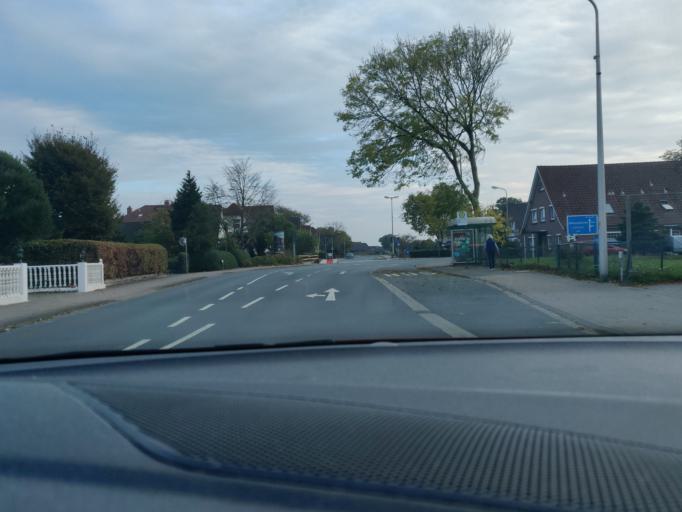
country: DE
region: Lower Saxony
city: Cuxhaven
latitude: 53.8632
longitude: 8.6357
